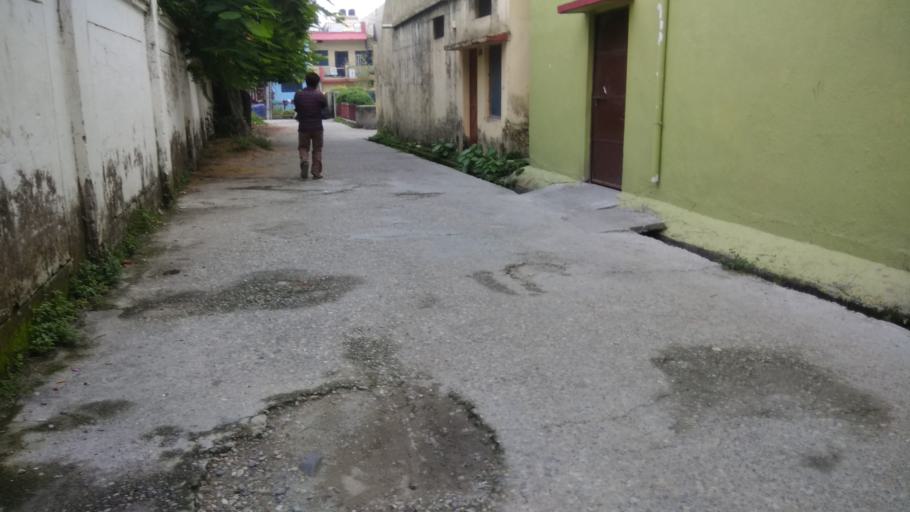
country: IN
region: Uttarakhand
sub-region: Dehradun
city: Raipur
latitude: 30.3128
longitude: 78.0628
